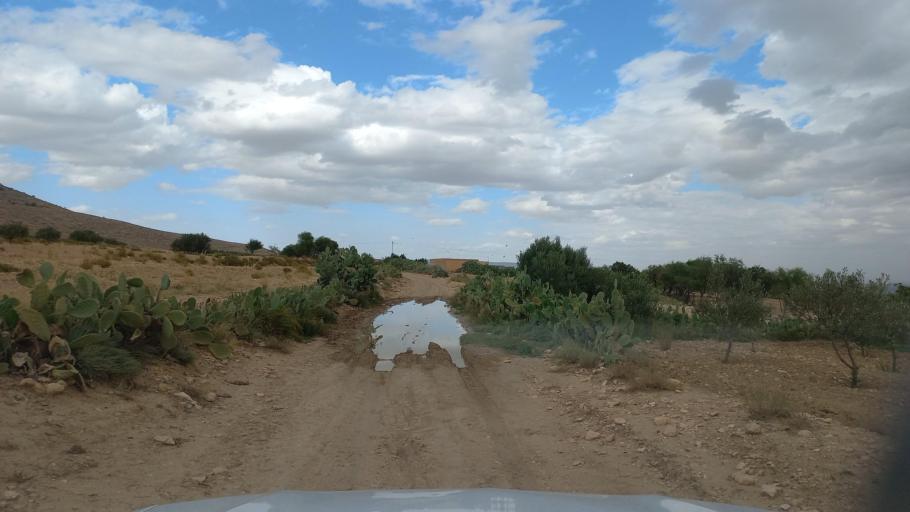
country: TN
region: Al Qasrayn
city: Sbiba
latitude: 35.4509
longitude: 9.0680
